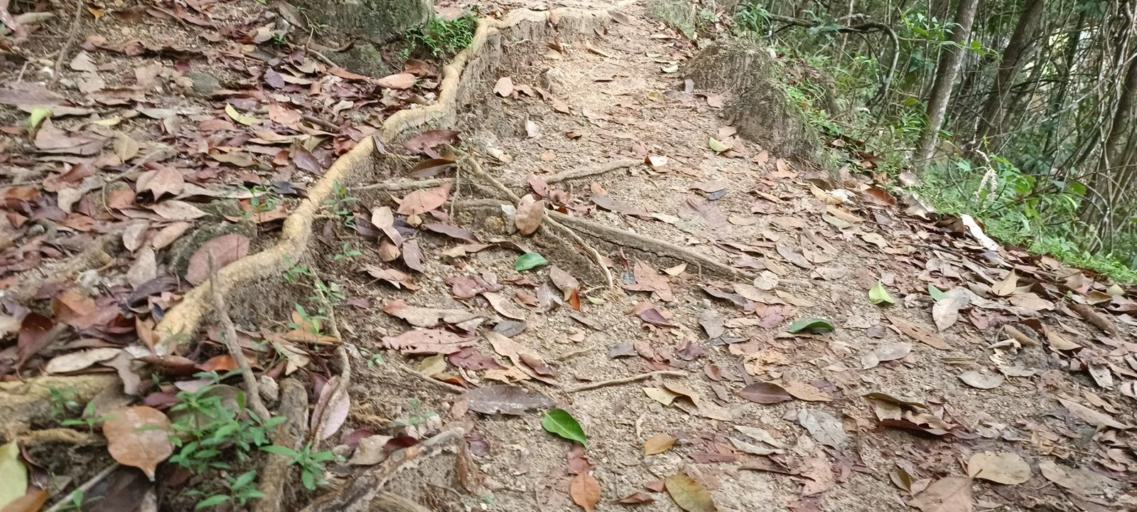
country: MY
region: Penang
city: George Town
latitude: 5.3887
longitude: 100.2918
